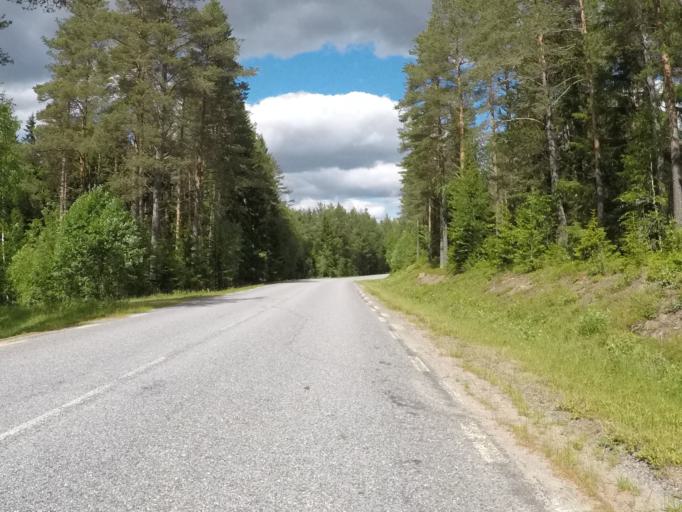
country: SE
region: Vaesterbotten
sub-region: Robertsfors Kommun
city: Robertsfors
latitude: 63.9790
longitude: 20.8106
